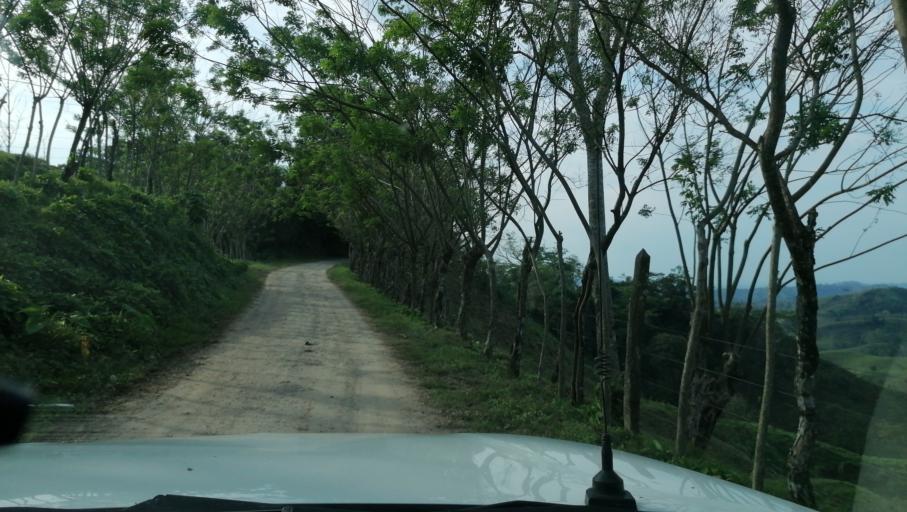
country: MX
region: Chiapas
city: Pichucalco
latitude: 17.4839
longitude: -93.2349
